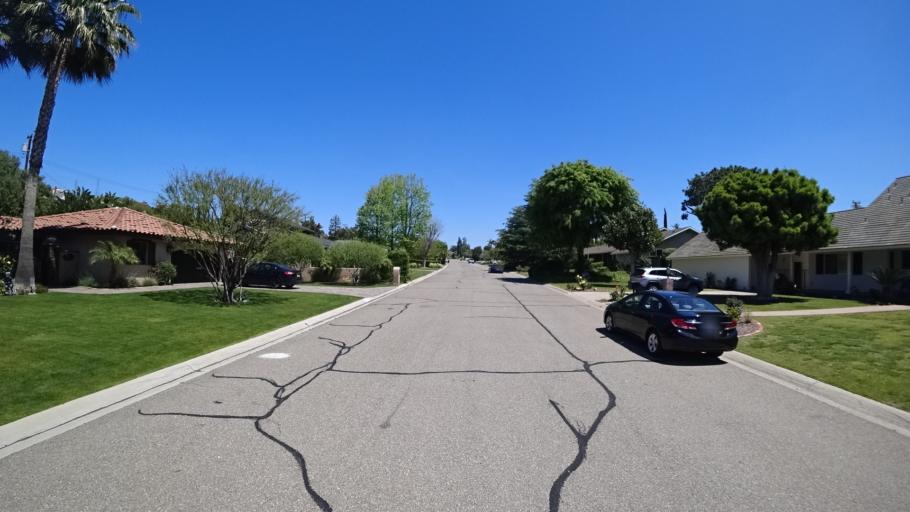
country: US
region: California
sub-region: Orange County
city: Villa Park
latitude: 33.8228
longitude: -117.8162
